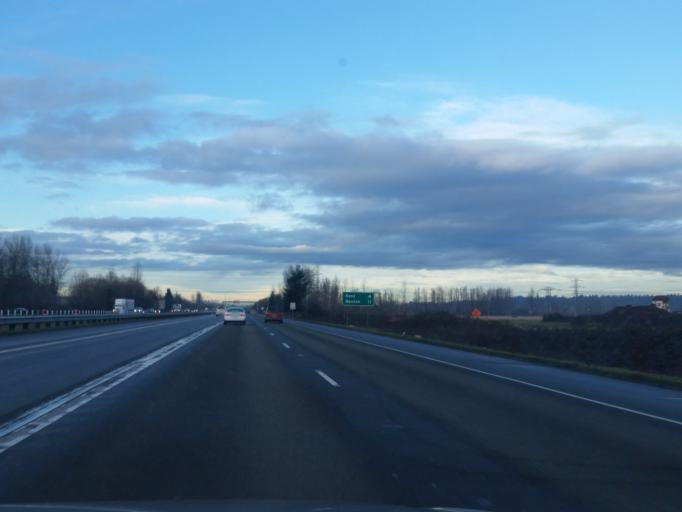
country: US
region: Washington
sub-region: King County
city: Auburn
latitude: 47.3296
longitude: -122.2446
